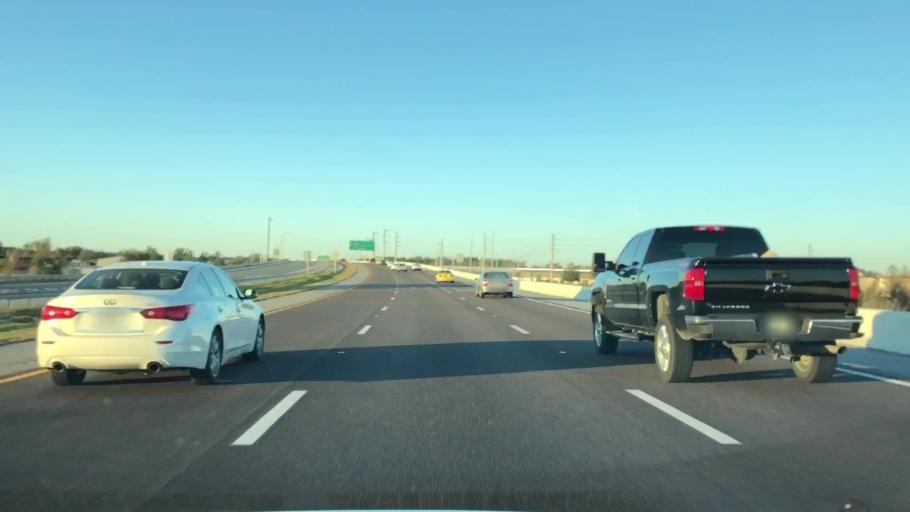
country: US
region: Florida
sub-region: Orange County
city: Apopka
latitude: 28.6866
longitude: -81.5584
